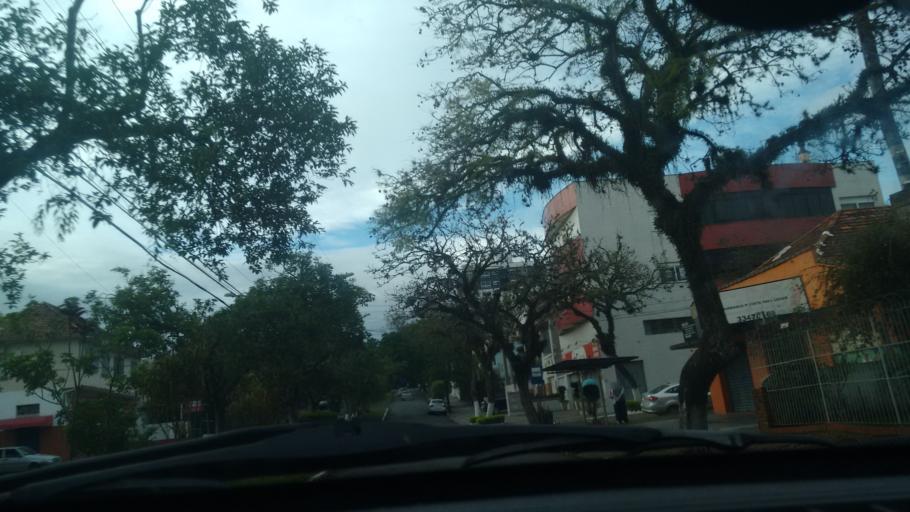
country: BR
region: Rio Grande do Sul
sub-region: Cachoeirinha
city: Cachoeirinha
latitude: -30.0022
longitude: -51.1460
